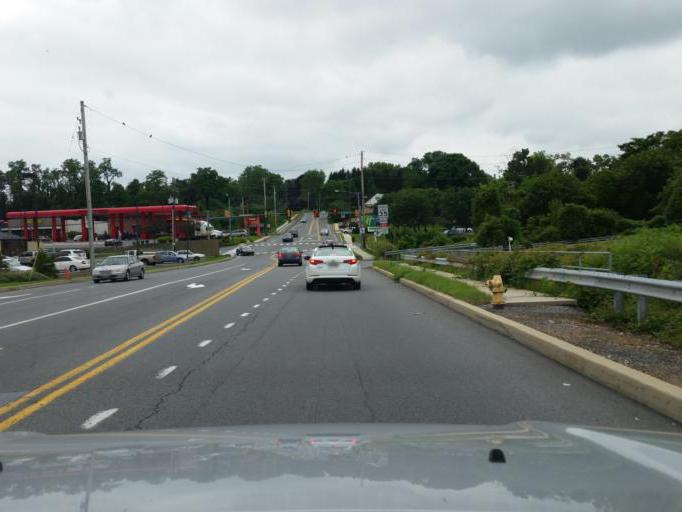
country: US
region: Pennsylvania
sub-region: Dauphin County
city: Hummelstown
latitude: 40.2695
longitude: -76.6897
